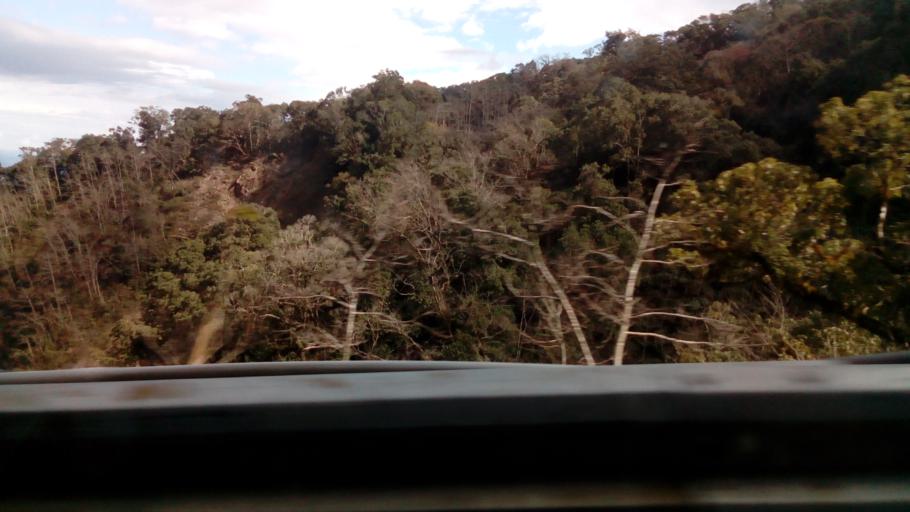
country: TW
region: Taiwan
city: Daxi
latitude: 24.4040
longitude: 121.3605
